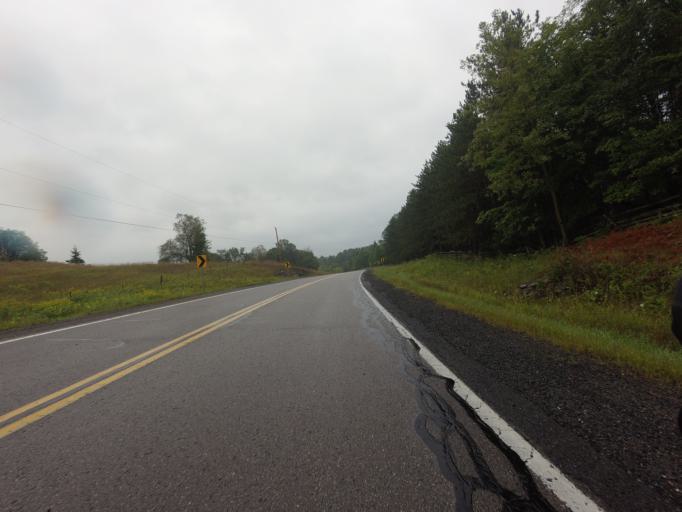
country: CA
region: Ontario
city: Perth
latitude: 45.0881
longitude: -76.4135
